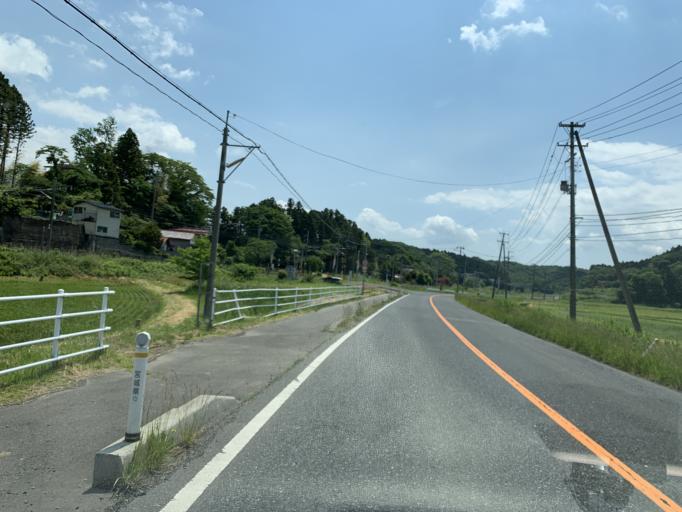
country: JP
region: Miyagi
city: Kogota
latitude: 38.4996
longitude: 141.0841
